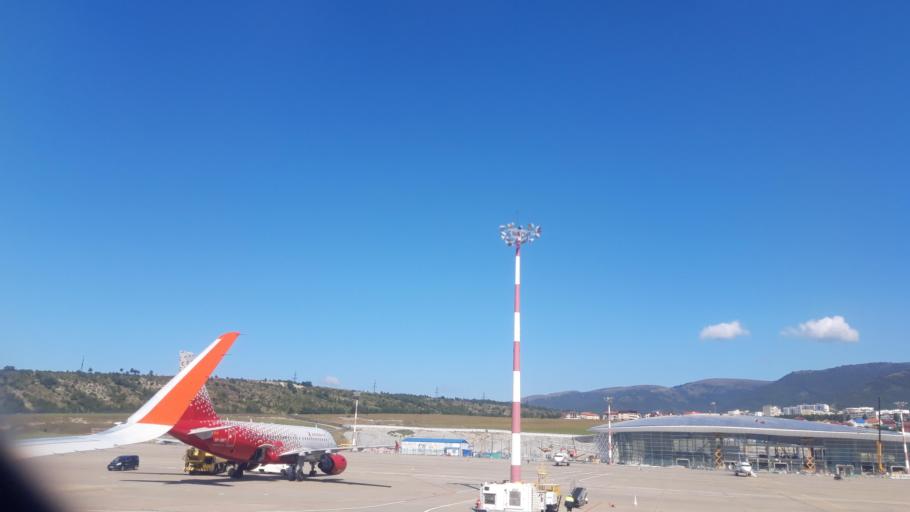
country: RU
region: Krasnodarskiy
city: Gelendzhik
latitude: 44.5922
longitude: 38.0222
